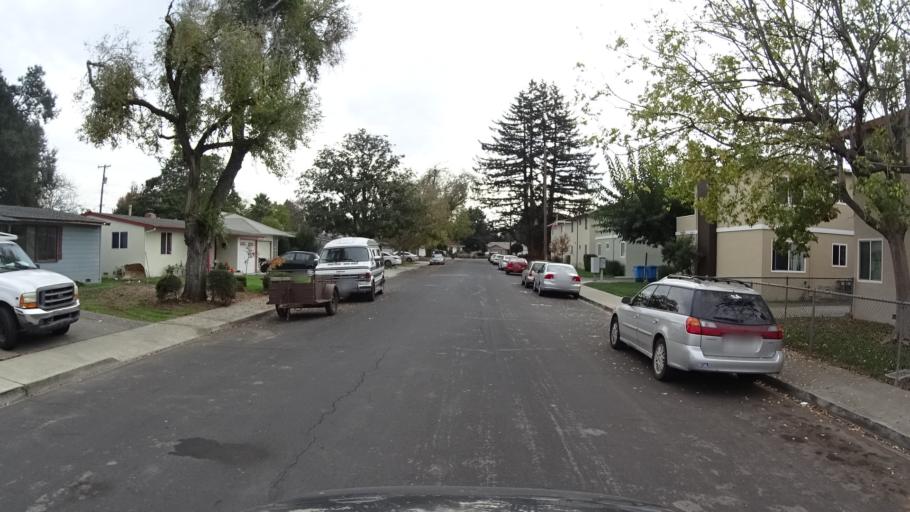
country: US
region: California
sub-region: Santa Clara County
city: Santa Clara
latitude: 37.3404
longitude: -121.9535
